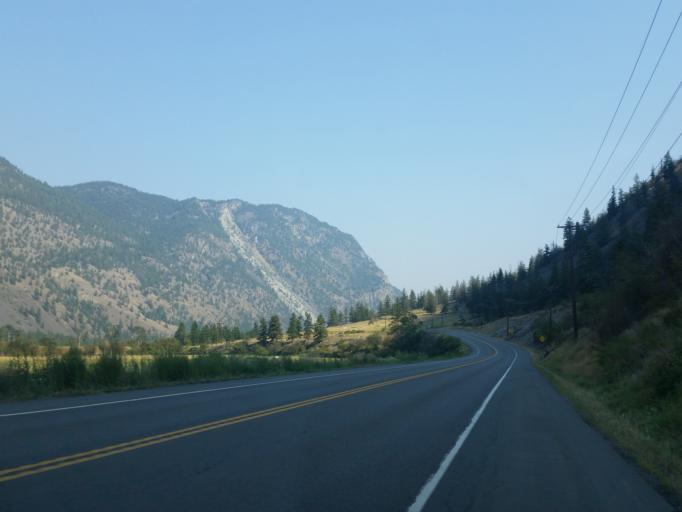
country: CA
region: British Columbia
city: Oliver
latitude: 49.2730
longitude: -120.0210
